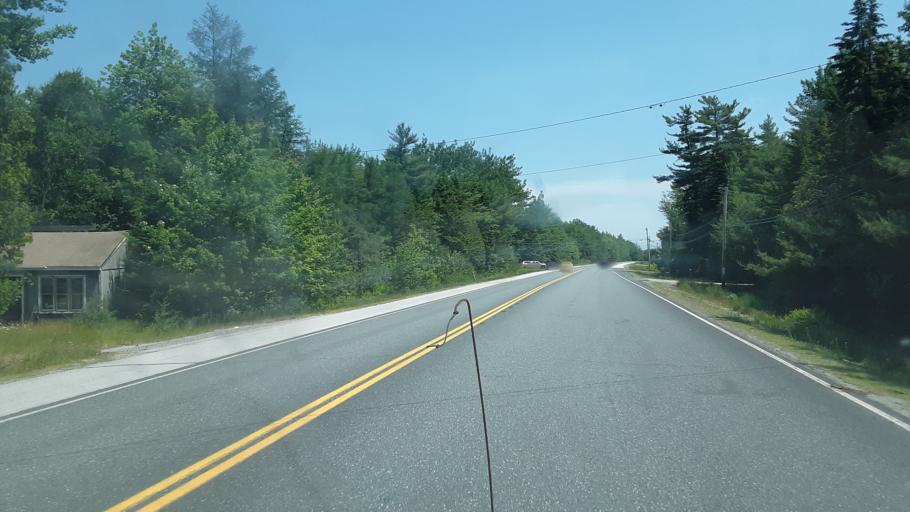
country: US
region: Maine
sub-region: Hancock County
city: Hancock
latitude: 44.5377
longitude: -68.2900
